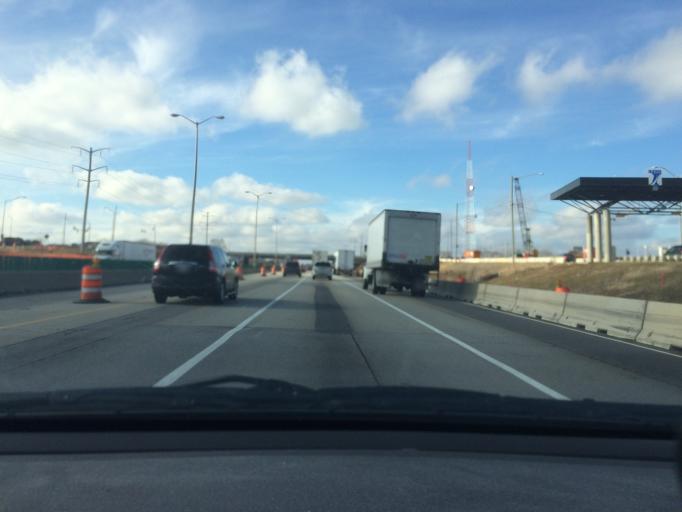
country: US
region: Illinois
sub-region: Cook County
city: Hoffman Estates
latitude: 42.0635
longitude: -88.0761
